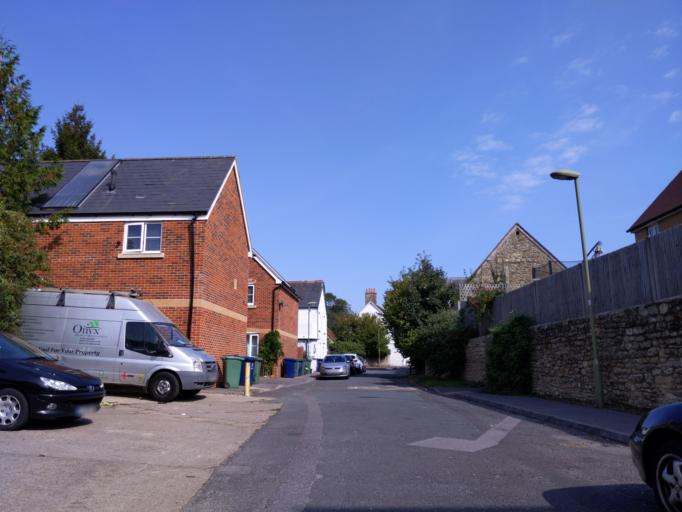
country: GB
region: England
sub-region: Oxfordshire
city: Cowley
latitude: 51.7205
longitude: -1.2261
